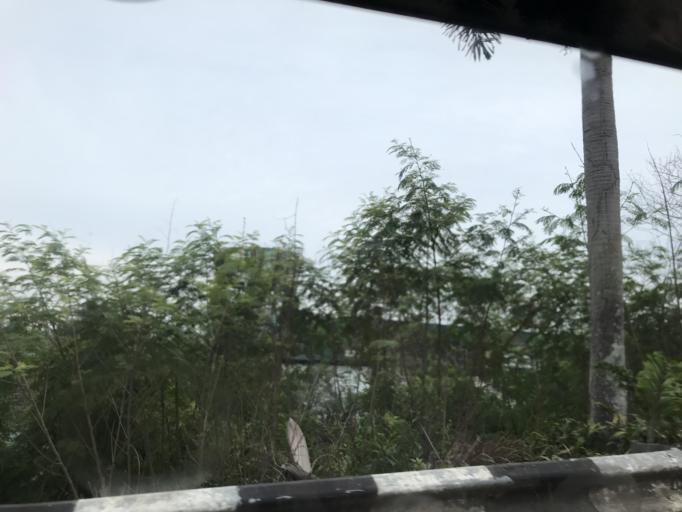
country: MY
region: Kelantan
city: Kota Bharu
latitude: 6.1222
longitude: 102.2053
